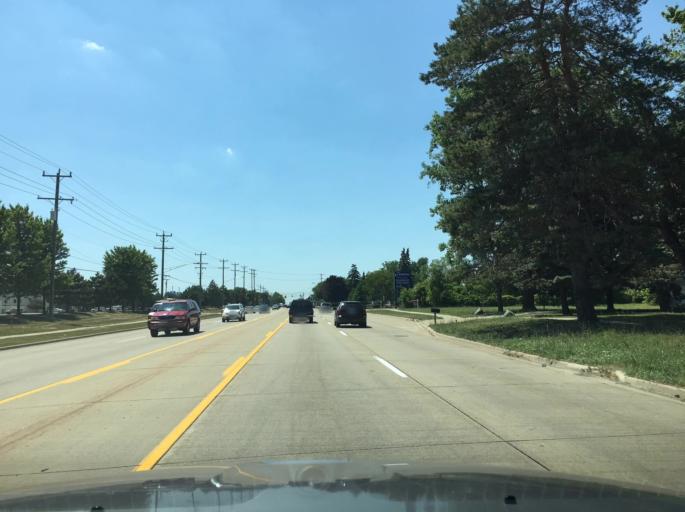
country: US
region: Michigan
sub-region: Macomb County
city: Clinton
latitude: 42.5545
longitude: -82.9062
